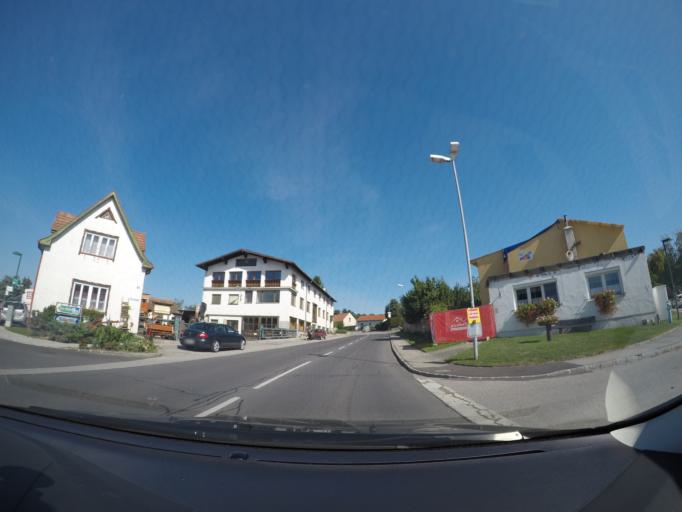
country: AT
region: Lower Austria
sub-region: Politischer Bezirk Bruck an der Leitha
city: Hof am Leithaberge
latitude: 47.9452
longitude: 16.5798
